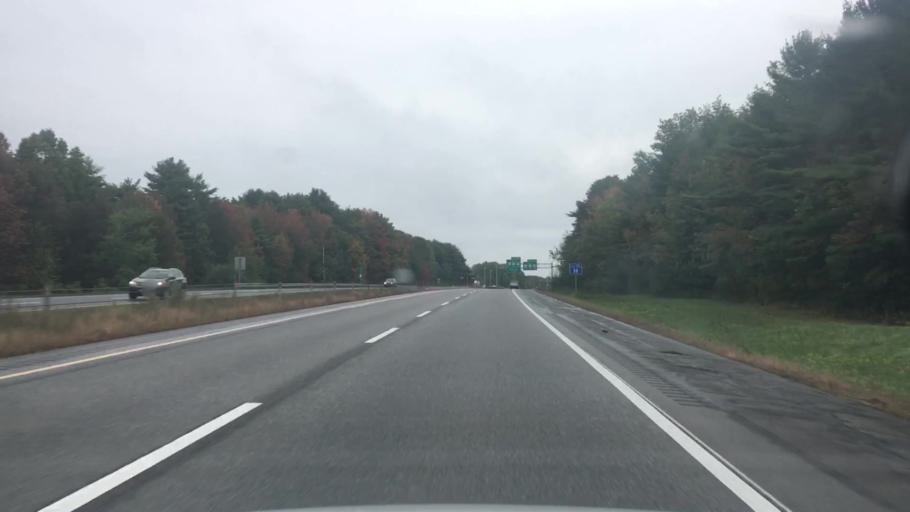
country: US
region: Maine
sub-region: Kennebec County
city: Augusta
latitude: 44.3420
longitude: -69.8017
